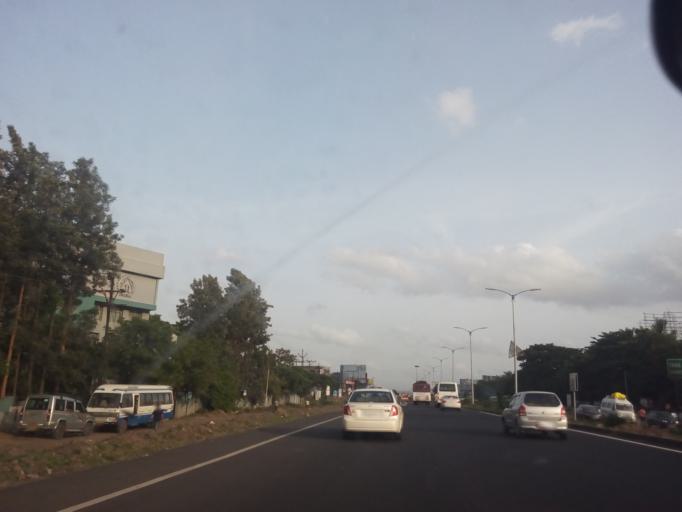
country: IN
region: Maharashtra
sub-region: Pune Division
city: Pimpri
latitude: 18.6114
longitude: 73.7500
